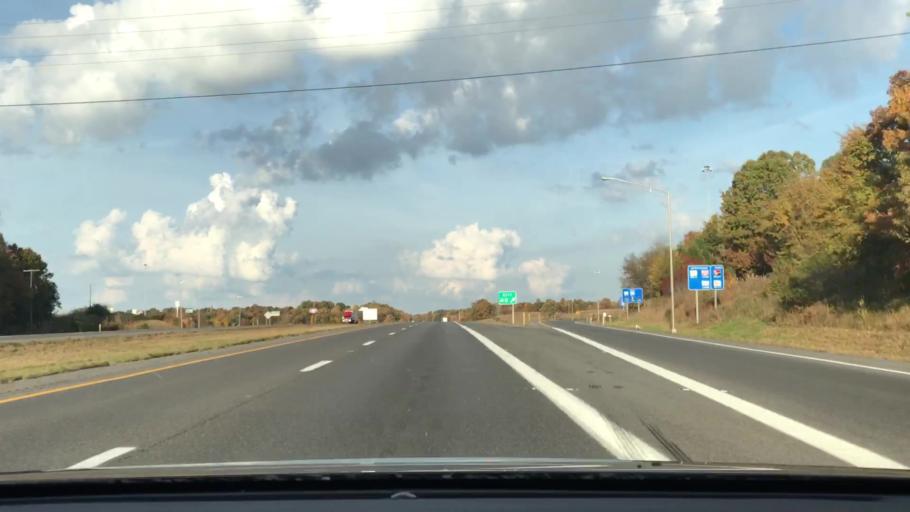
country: US
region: Kentucky
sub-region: Lyon County
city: Eddyville
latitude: 37.0728
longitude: -88.1162
